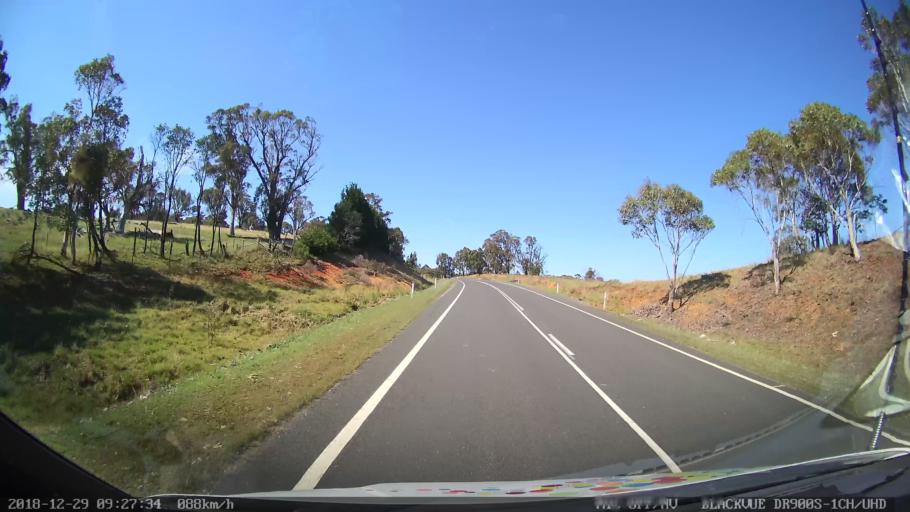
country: AU
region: New South Wales
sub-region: Upper Lachlan Shire
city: Crookwell
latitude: -34.5681
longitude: 149.3842
